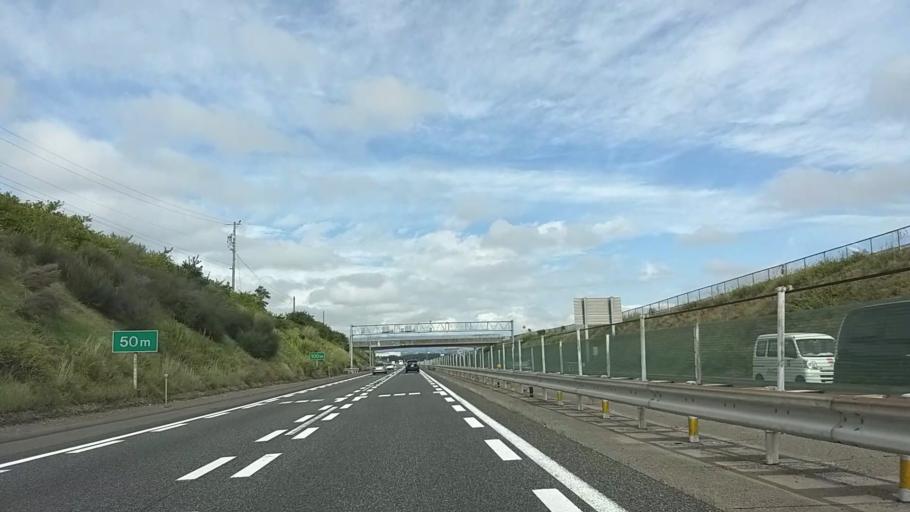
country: JP
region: Nagano
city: Shiojiri
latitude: 36.1250
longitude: 137.9772
